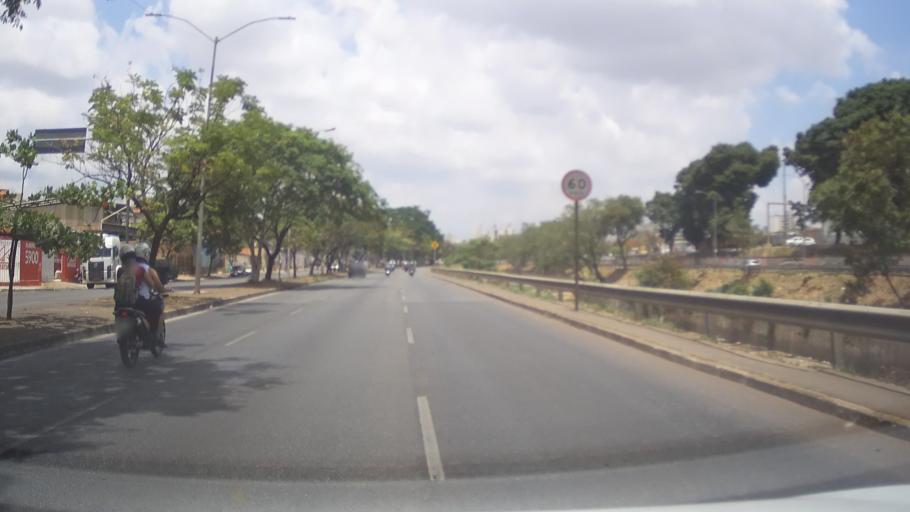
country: BR
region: Minas Gerais
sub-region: Belo Horizonte
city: Belo Horizonte
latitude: -19.9024
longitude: -43.9072
